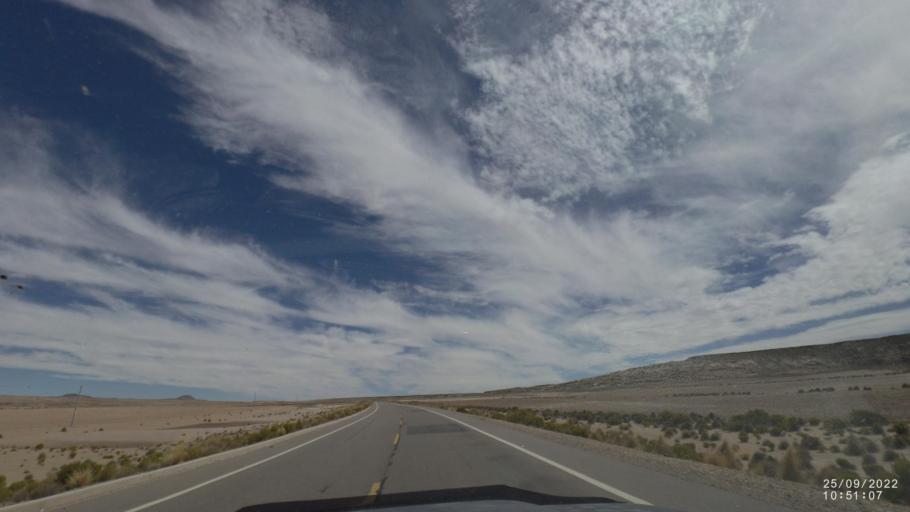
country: BO
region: Oruro
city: Challapata
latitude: -19.5660
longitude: -66.8446
